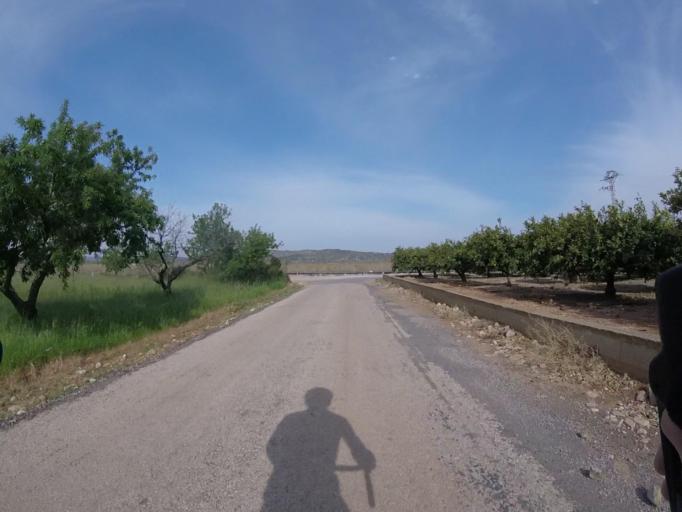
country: ES
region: Valencia
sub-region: Provincia de Castello
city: Alcoceber
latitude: 40.2596
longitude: 0.2530
